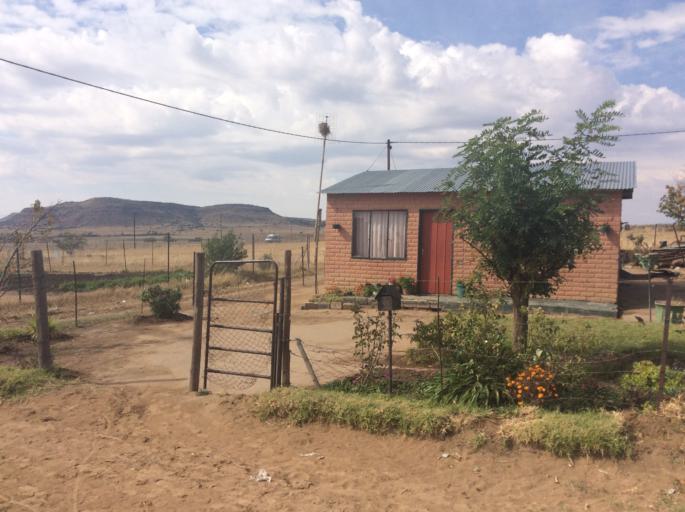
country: ZA
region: Orange Free State
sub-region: Xhariep District Municipality
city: Dewetsdorp
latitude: -29.5795
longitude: 26.6915
